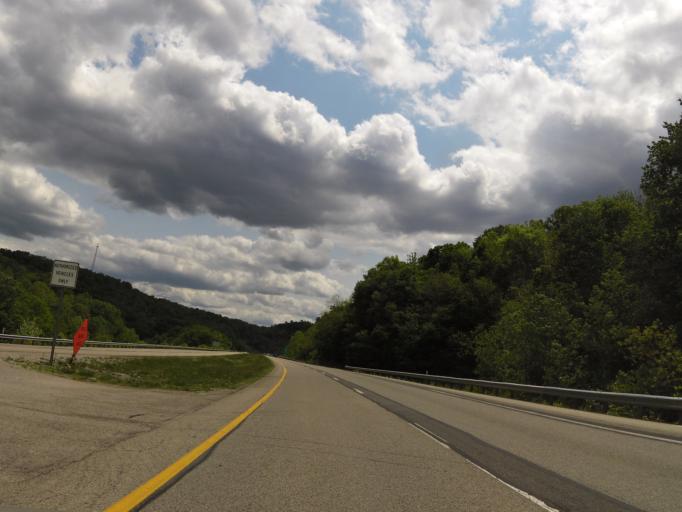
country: US
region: West Virginia
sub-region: Kanawha County
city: Charleston
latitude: 38.4328
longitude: -81.6258
